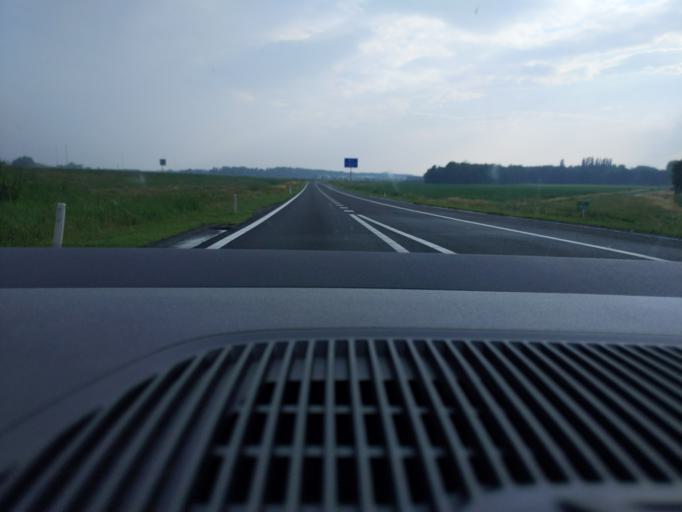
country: NL
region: Groningen
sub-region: Gemeente Veendam
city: Veendam
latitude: 53.1720
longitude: 6.8914
